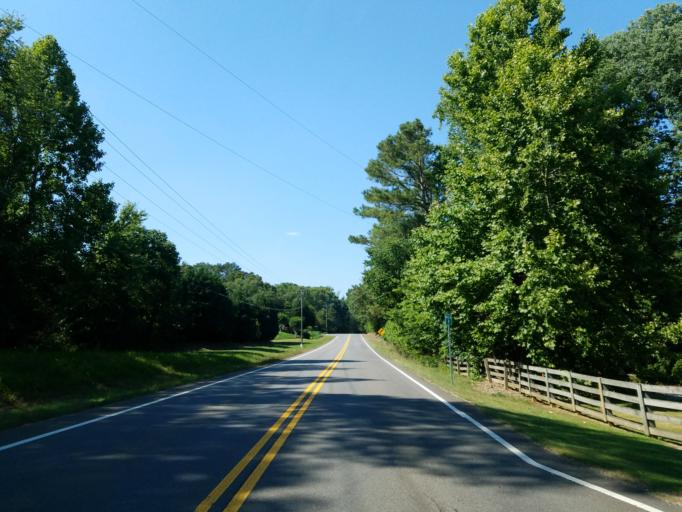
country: US
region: Georgia
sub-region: Fulton County
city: Milton
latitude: 34.1966
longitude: -84.3063
